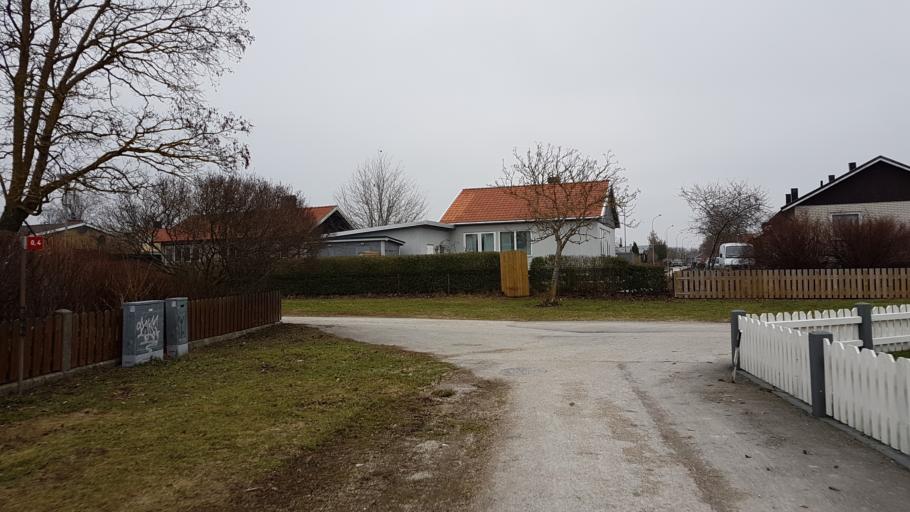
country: SE
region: Gotland
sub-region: Gotland
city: Visby
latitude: 57.6359
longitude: 18.3182
